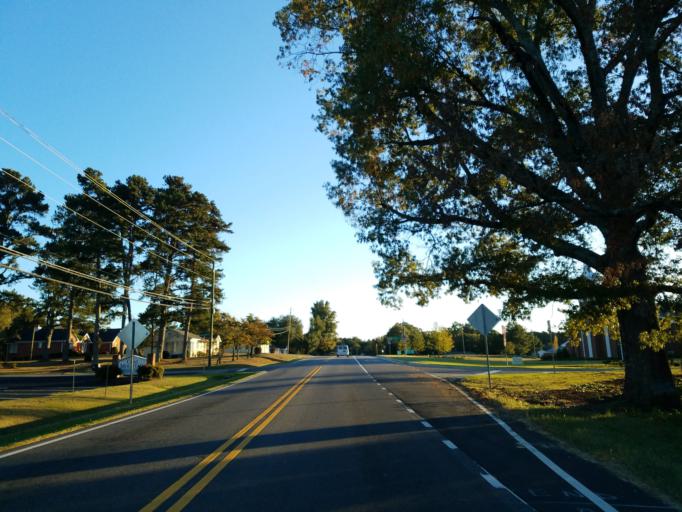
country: US
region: Georgia
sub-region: Forsyth County
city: Cumming
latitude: 34.2700
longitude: -84.1014
